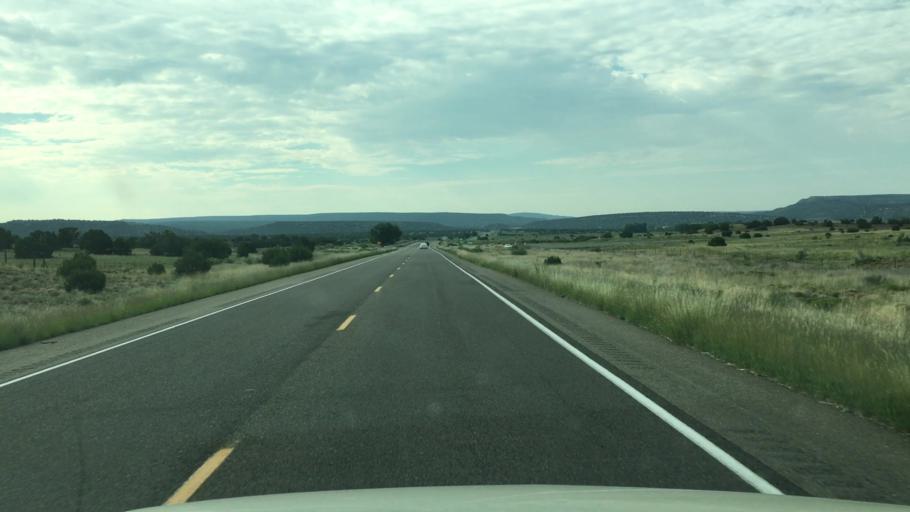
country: US
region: New Mexico
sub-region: Santa Fe County
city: Eldorado at Santa Fe
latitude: 35.4161
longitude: -105.8698
